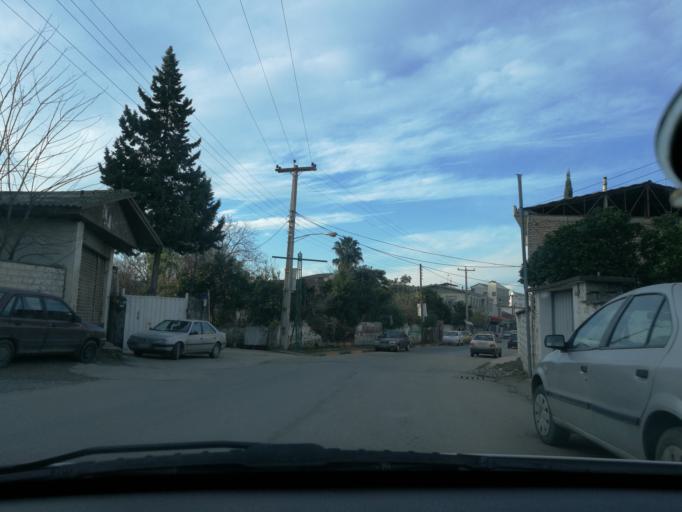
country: IR
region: Mazandaran
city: Chalus
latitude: 36.6468
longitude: 51.4301
